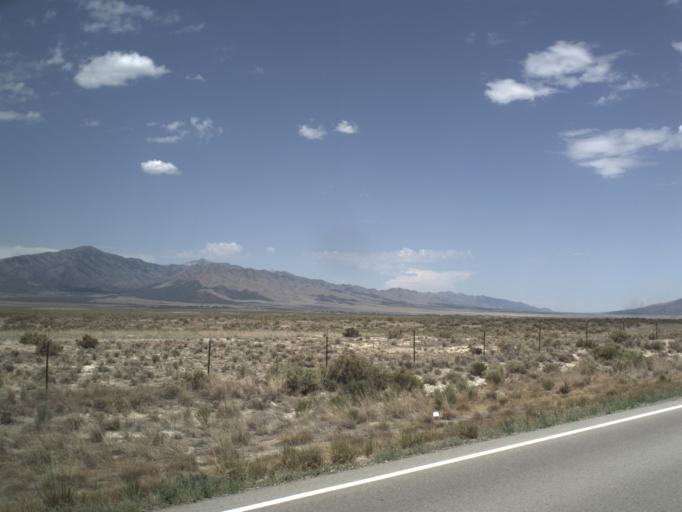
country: US
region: Utah
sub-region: Tooele County
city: Tooele
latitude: 40.2594
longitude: -112.3982
